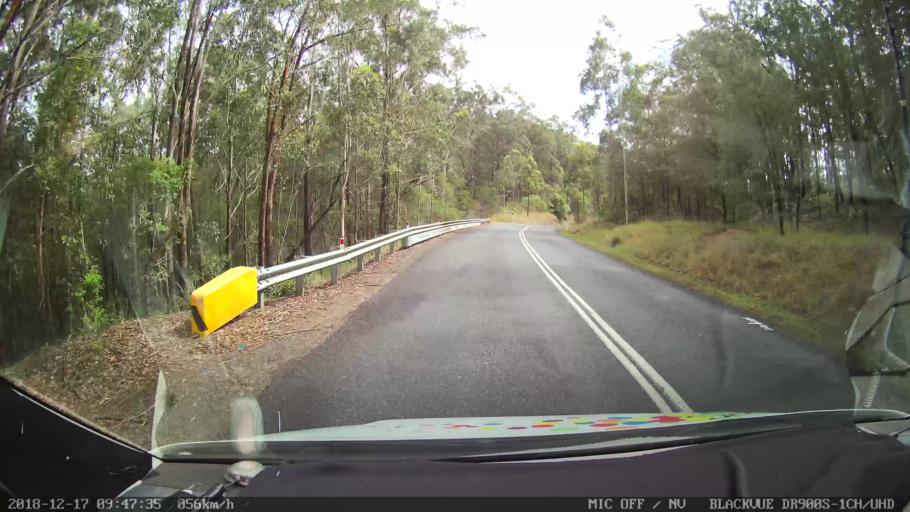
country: AU
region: New South Wales
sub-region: Tenterfield Municipality
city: Carrolls Creek
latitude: -28.9276
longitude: 152.3388
